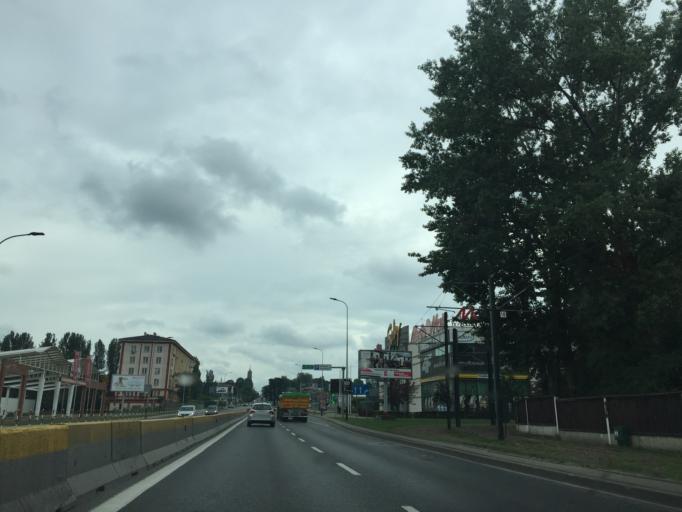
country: PL
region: Lesser Poland Voivodeship
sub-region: Krakow
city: Krakow
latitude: 50.0151
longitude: 19.9291
